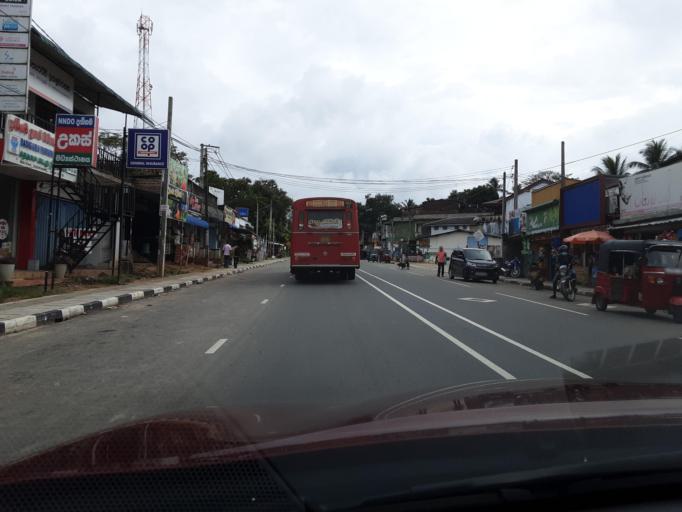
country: LK
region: Eastern Province
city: Ampara
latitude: 7.4035
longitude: 81.2435
